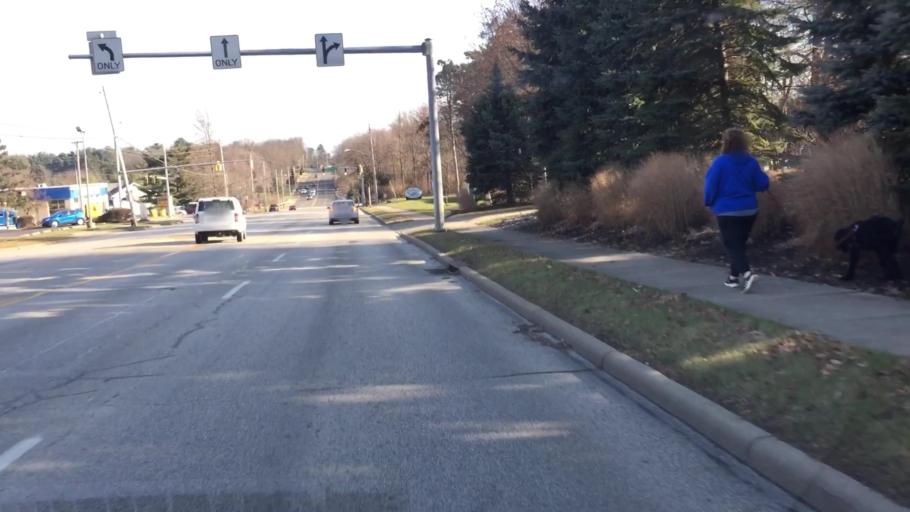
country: US
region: Ohio
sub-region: Summit County
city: Stow
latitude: 41.1551
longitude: -81.4002
